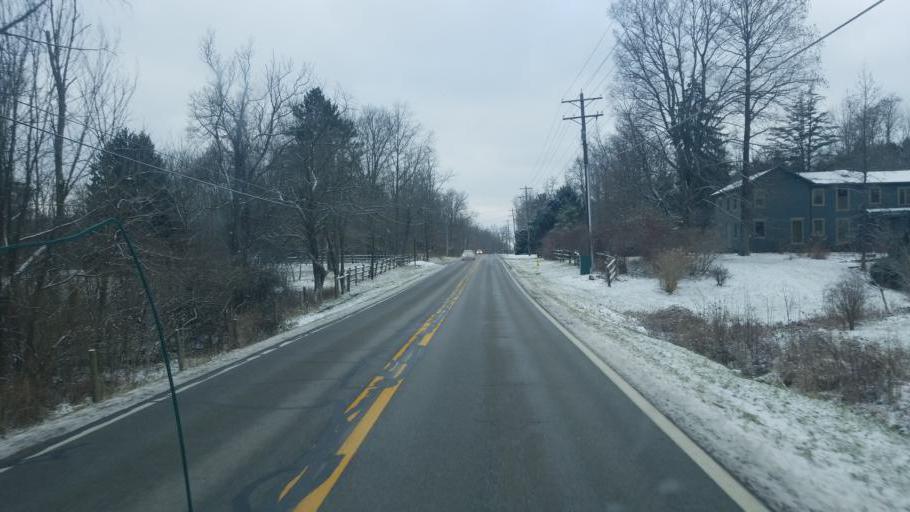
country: US
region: Ohio
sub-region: Franklin County
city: Gahanna
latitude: 40.0319
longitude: -82.8464
